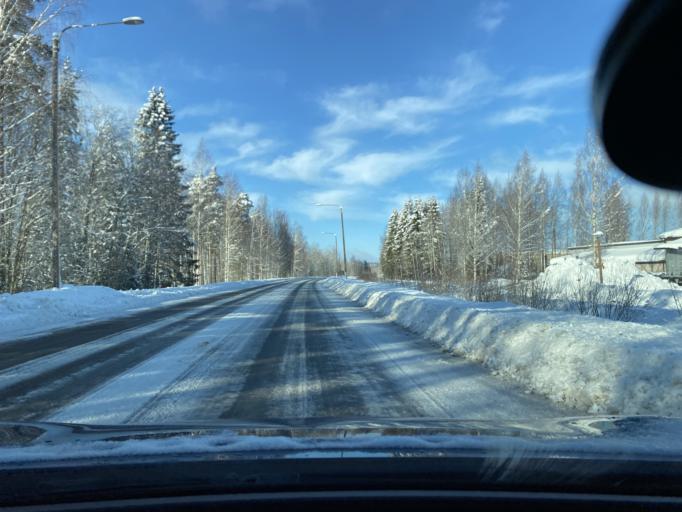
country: FI
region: Southern Savonia
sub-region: Mikkeli
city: Kangasniemi
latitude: 62.0052
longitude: 26.6481
